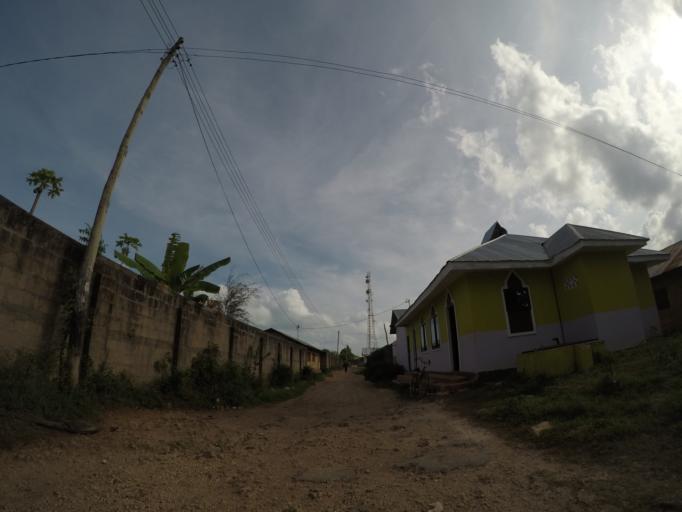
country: TZ
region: Zanzibar Central/South
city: Koani
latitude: -6.2260
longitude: 39.3167
